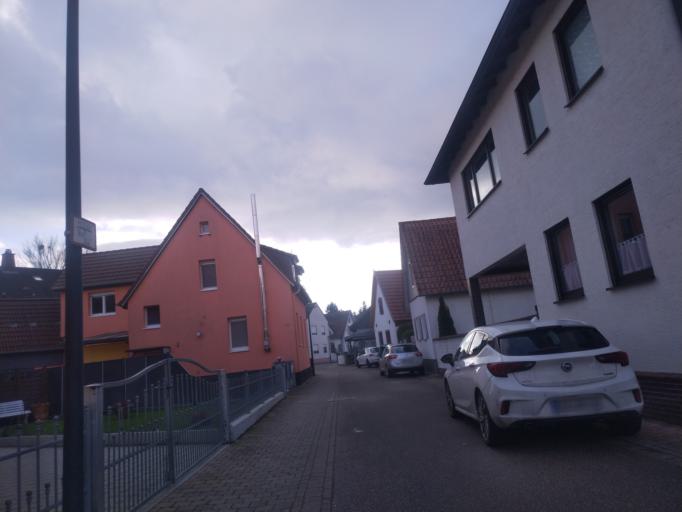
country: DE
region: Rheinland-Pfalz
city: Worth am Rhein
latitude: 49.0306
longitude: 8.2878
